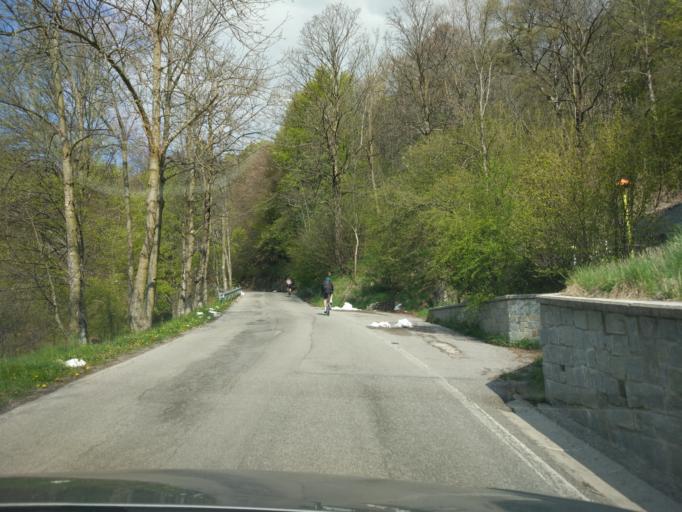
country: IT
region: Lombardy
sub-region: Provincia di Lecco
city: Ballabio
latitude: 45.9063
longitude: 9.3979
